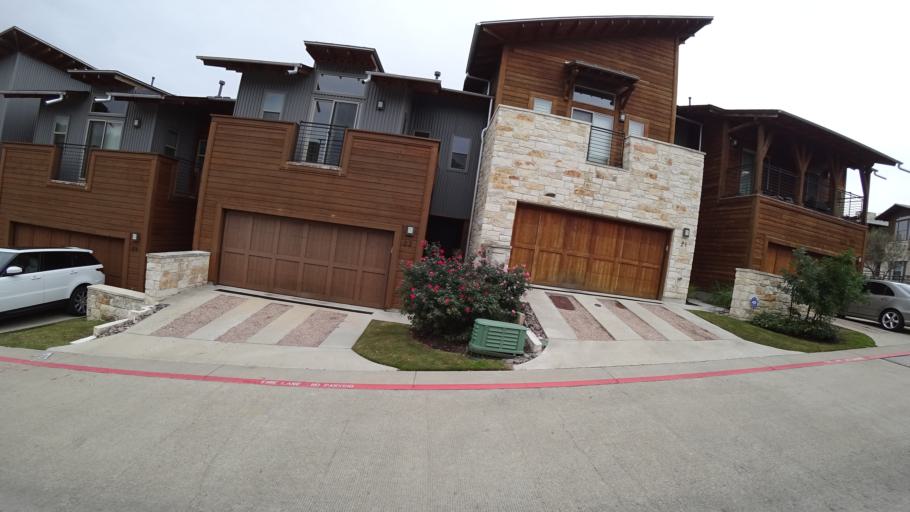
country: US
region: Texas
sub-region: Williamson County
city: Jollyville
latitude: 30.3800
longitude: -97.8050
